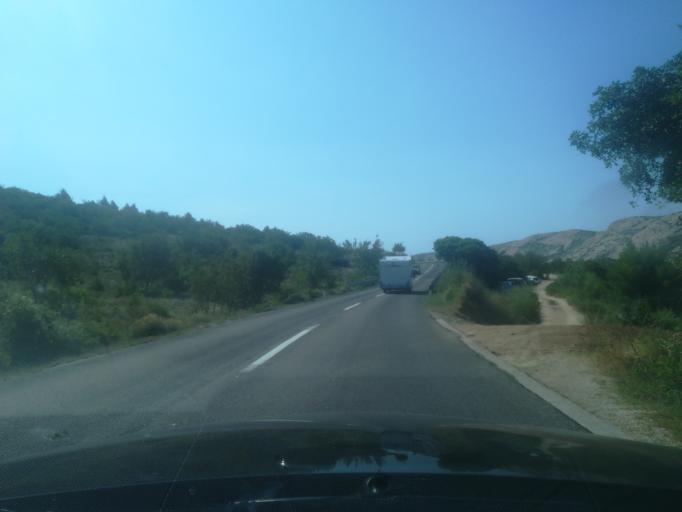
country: HR
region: Primorsko-Goranska
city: Banjol
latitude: 44.7140
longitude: 14.8276
